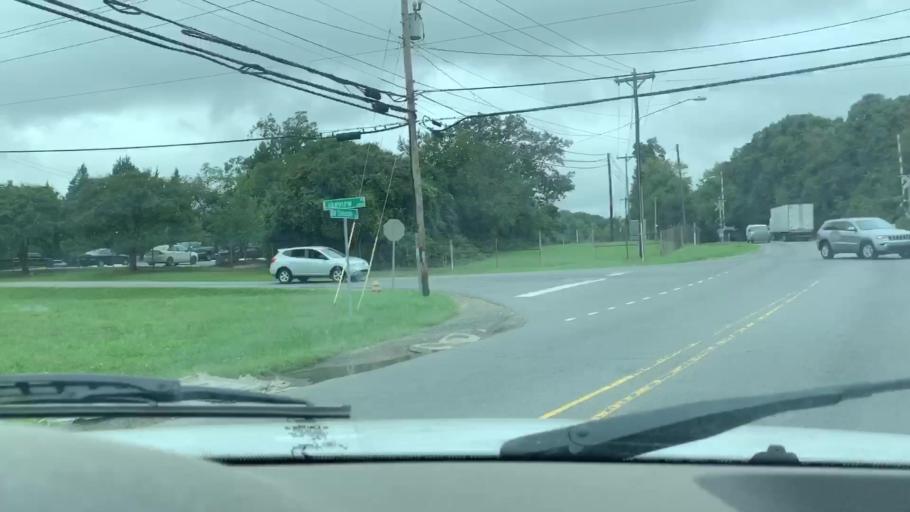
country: US
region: North Carolina
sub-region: Mecklenburg County
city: Huntersville
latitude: 35.3386
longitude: -80.8242
